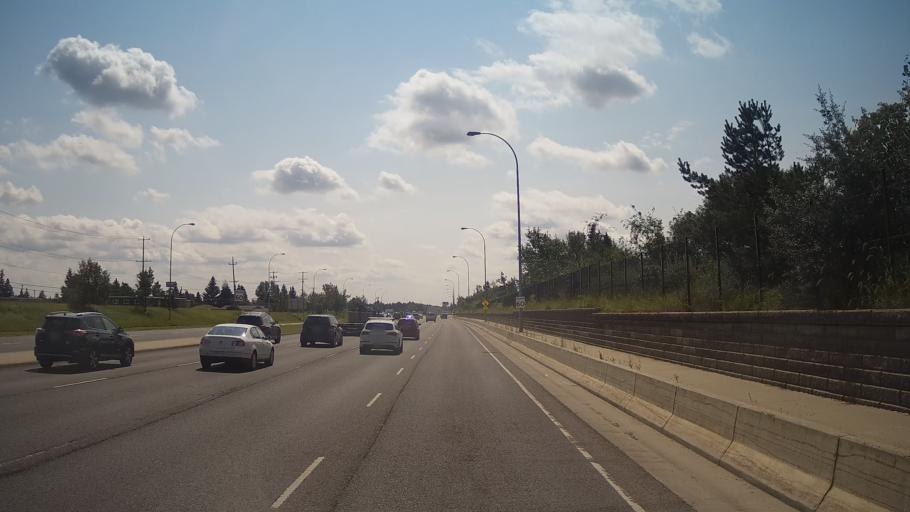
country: CA
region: Alberta
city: St. Albert
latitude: 53.5189
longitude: -113.6156
